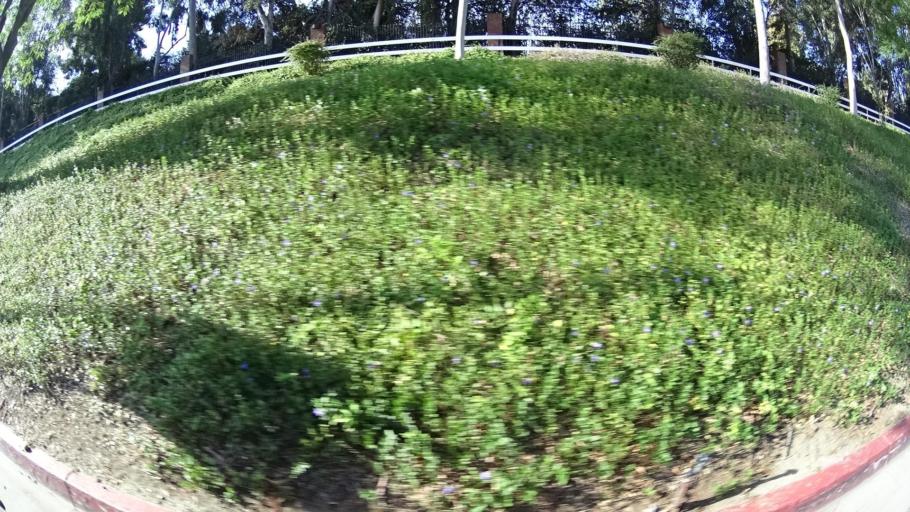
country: US
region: California
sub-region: Los Angeles County
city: South San Jose Hills
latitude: 34.0250
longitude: -117.9219
